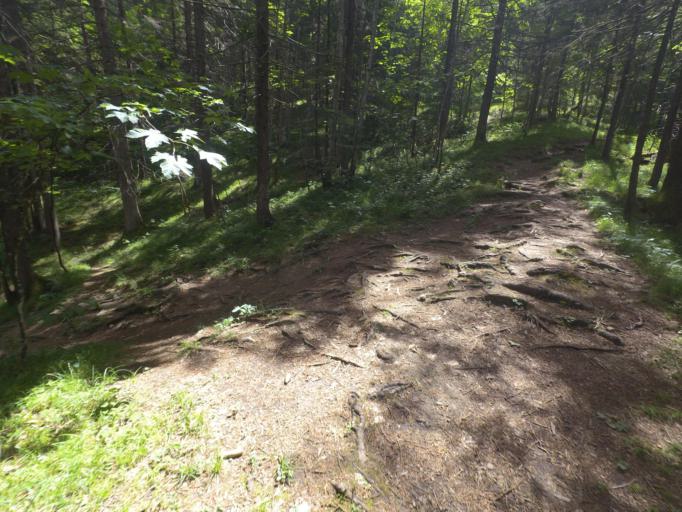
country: AT
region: Salzburg
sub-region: Politischer Bezirk Zell am See
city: Saalfelden am Steinernen Meer
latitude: 47.4463
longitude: 12.8563
